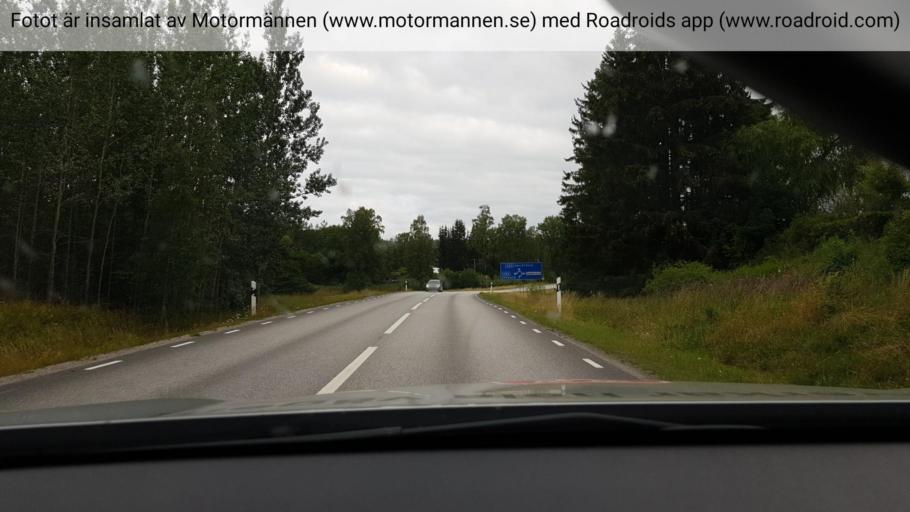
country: SE
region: Stockholm
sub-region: Norrtalje Kommun
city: Skanninge
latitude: 59.8913
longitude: 18.4910
